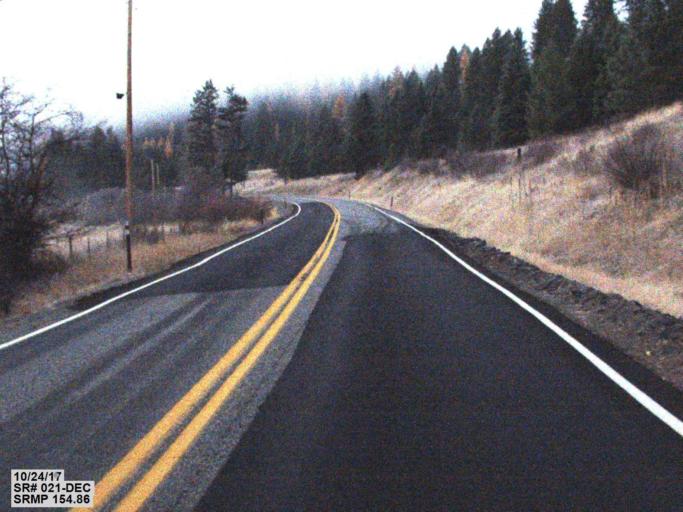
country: US
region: Washington
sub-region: Ferry County
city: Republic
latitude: 48.5682
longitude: -118.7482
